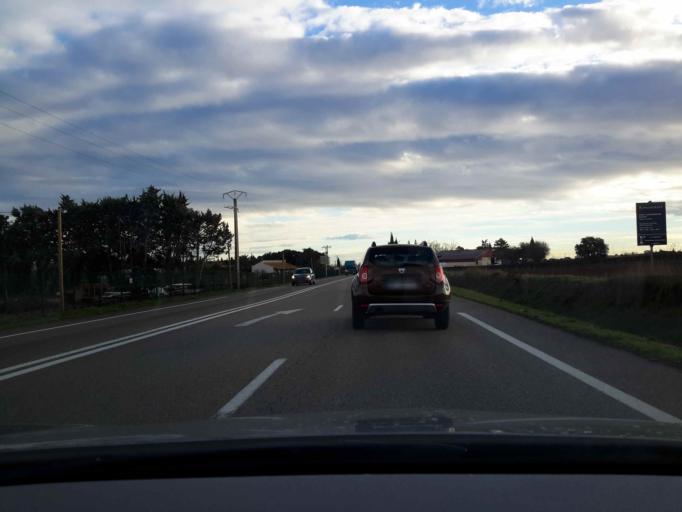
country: FR
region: Languedoc-Roussillon
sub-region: Departement du Gard
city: Caissargues
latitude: 43.7814
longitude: 4.3511
